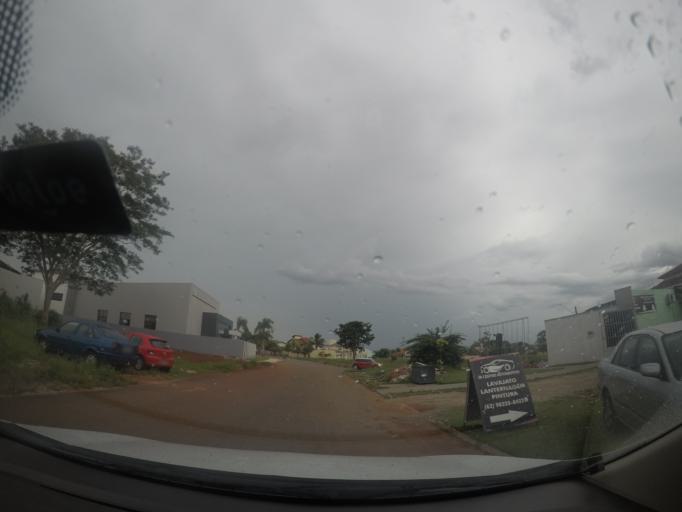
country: BR
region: Goias
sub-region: Goiania
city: Goiania
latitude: -16.6413
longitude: -49.2295
